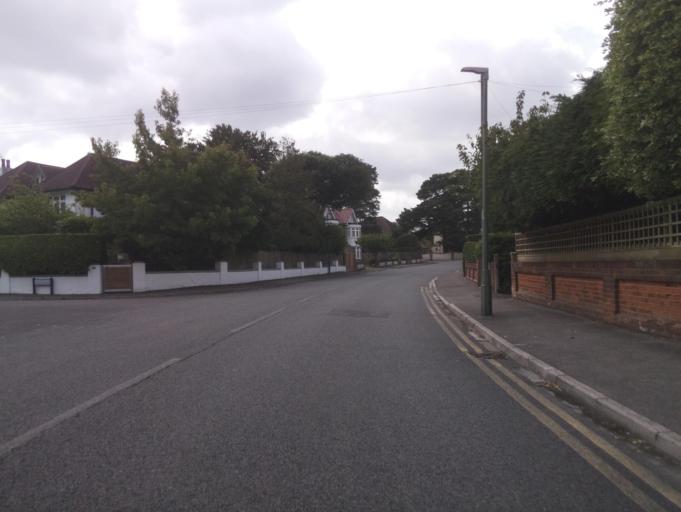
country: GB
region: England
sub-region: Bournemouth
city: Bournemouth
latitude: 50.7133
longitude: -1.9036
